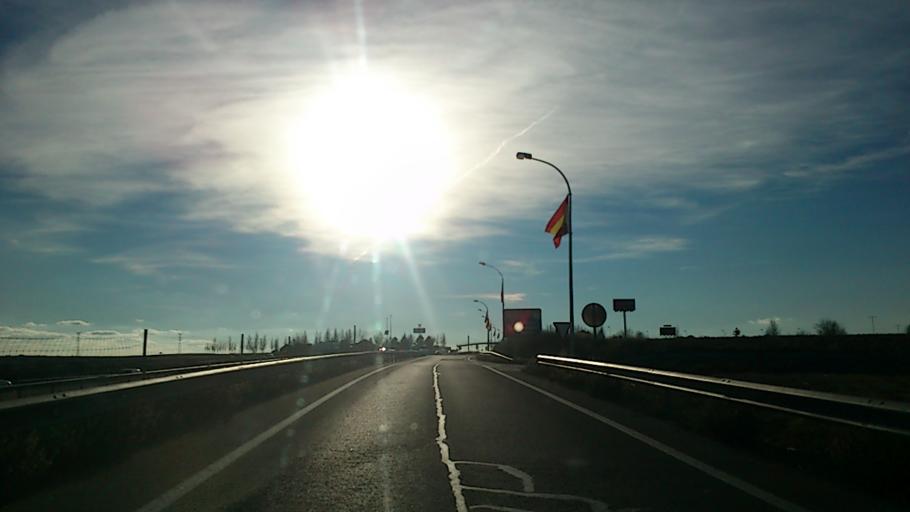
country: ES
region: Castille-La Mancha
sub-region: Provincia de Guadalajara
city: Almadrones
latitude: 40.8998
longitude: -2.7557
